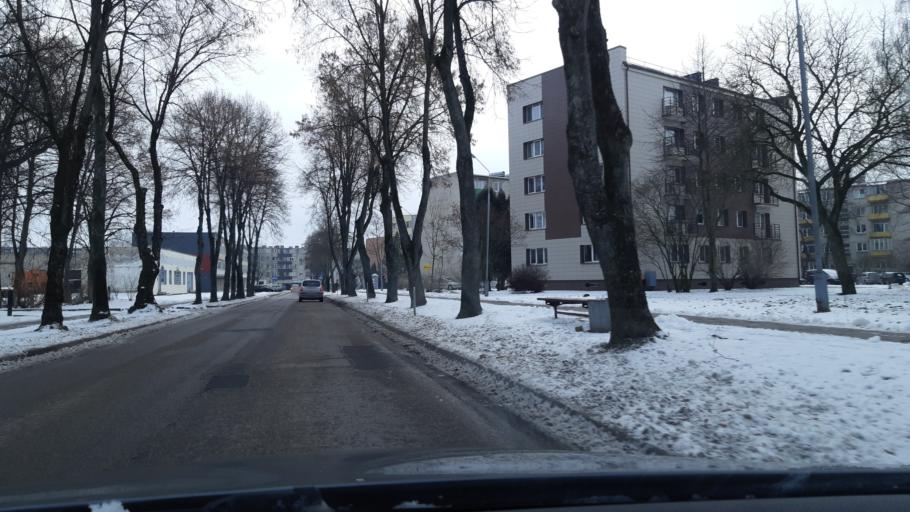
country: LT
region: Kauno apskritis
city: Kedainiai
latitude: 55.2914
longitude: 23.9810
